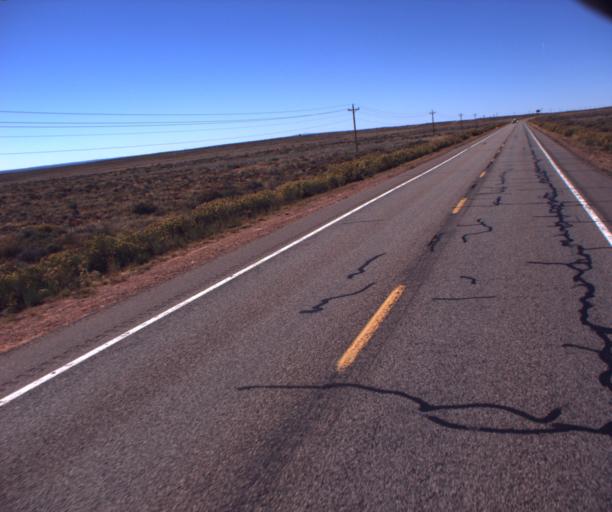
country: US
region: Arizona
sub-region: Coconino County
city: Fredonia
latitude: 36.8845
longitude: -112.6342
